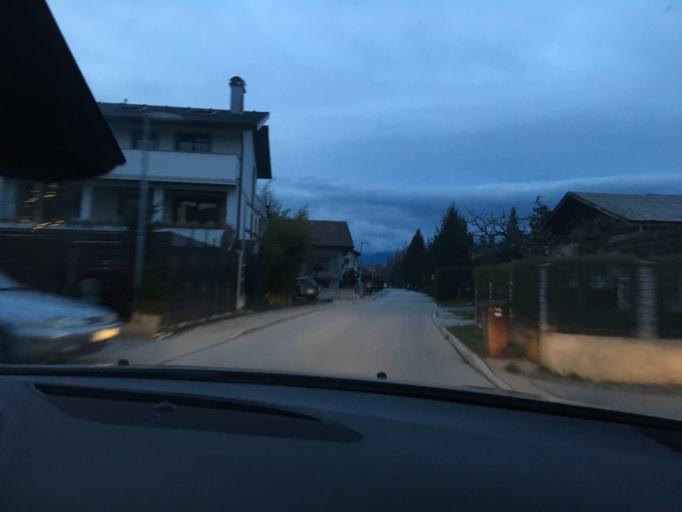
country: SI
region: Domzale
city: Vir
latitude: 46.1506
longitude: 14.6063
